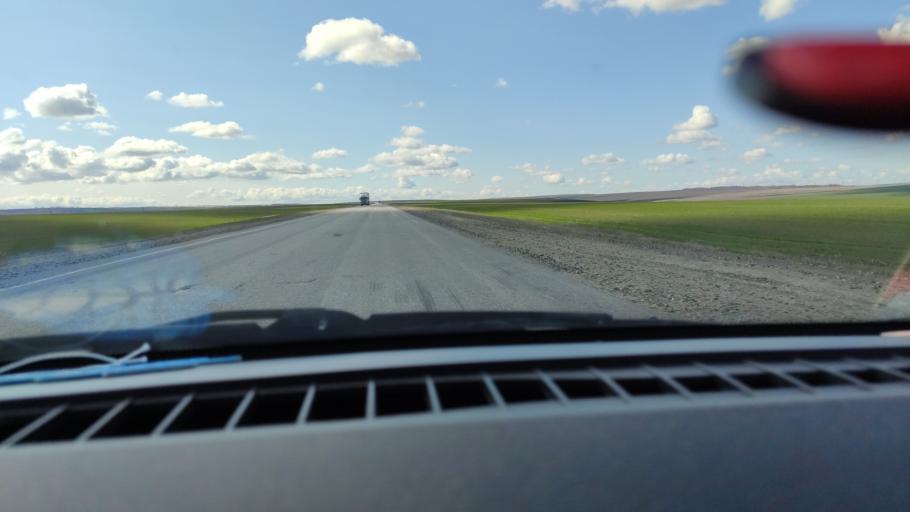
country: RU
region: Samara
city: Varlamovo
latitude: 53.0480
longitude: 48.3434
